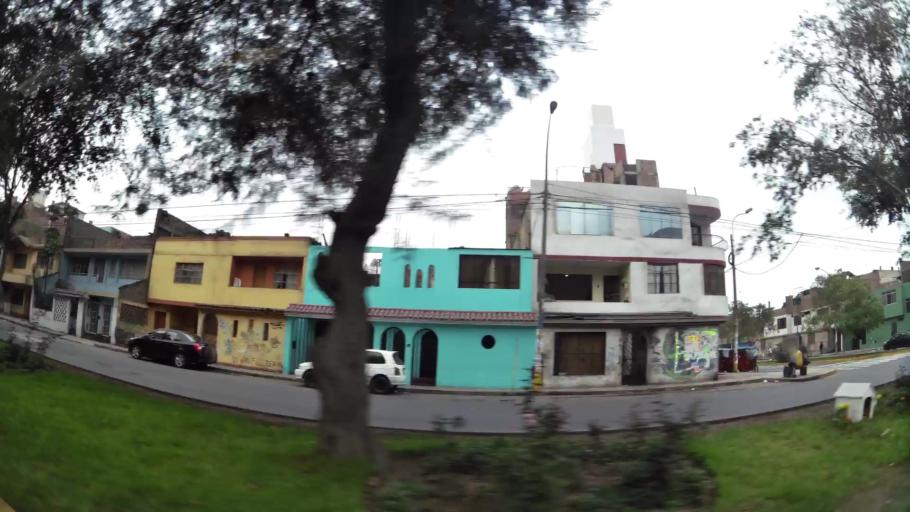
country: PE
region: Lima
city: Lima
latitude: -12.0204
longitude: -77.0125
